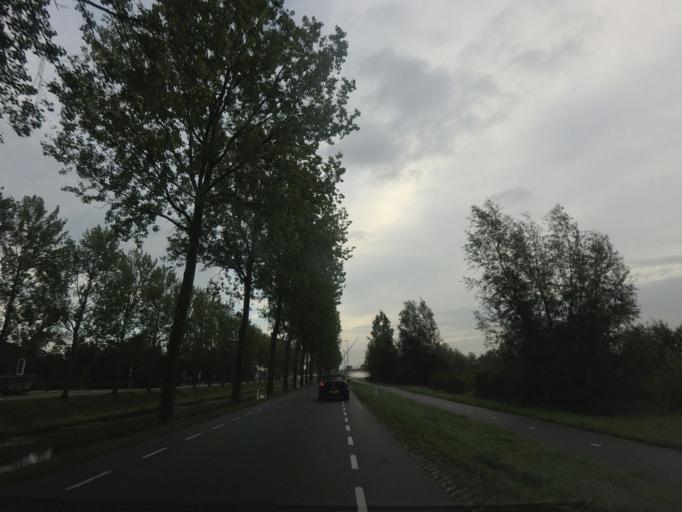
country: NL
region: North Holland
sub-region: Gemeente Haarlemmermeer
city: Hoofddorp
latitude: 52.2882
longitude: 4.6680
